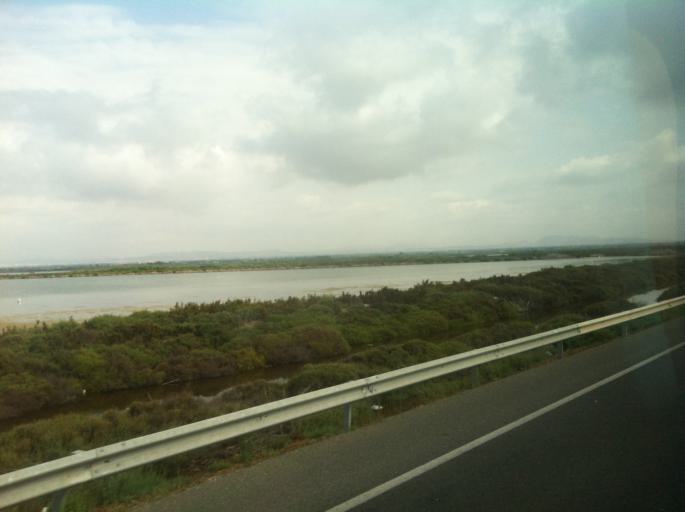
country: ES
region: Valencia
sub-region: Provincia de Alicante
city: Santa Pola
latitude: 38.1812
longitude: -0.6177
